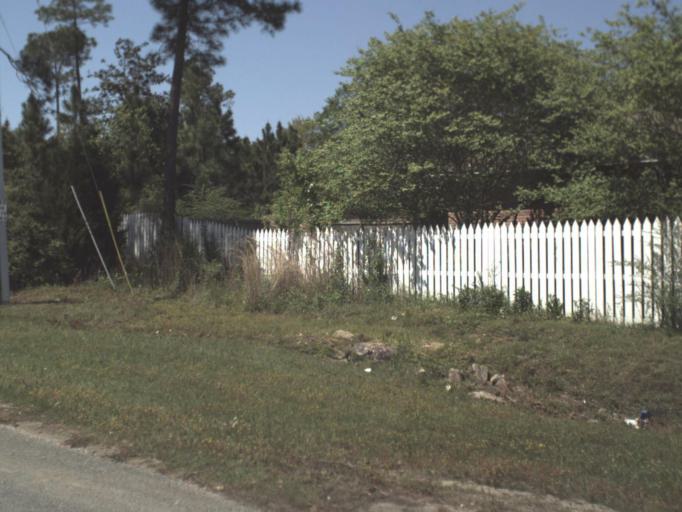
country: US
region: Florida
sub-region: Escambia County
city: Bellview
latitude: 30.4946
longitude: -87.3270
